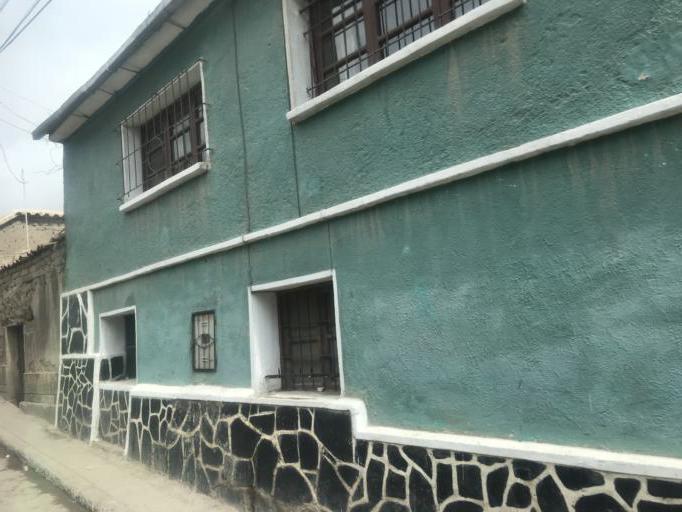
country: BO
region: Potosi
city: Potosi
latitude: -19.5996
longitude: -65.7481
